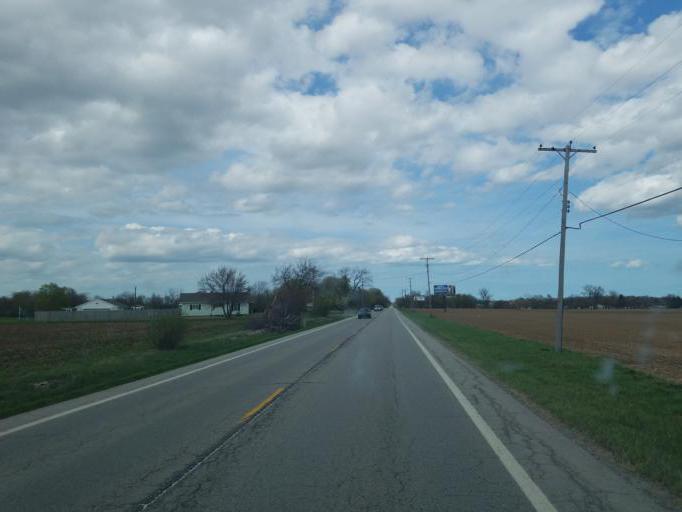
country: US
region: Ohio
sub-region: Erie County
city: Sandusky
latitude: 41.3540
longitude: -82.7528
